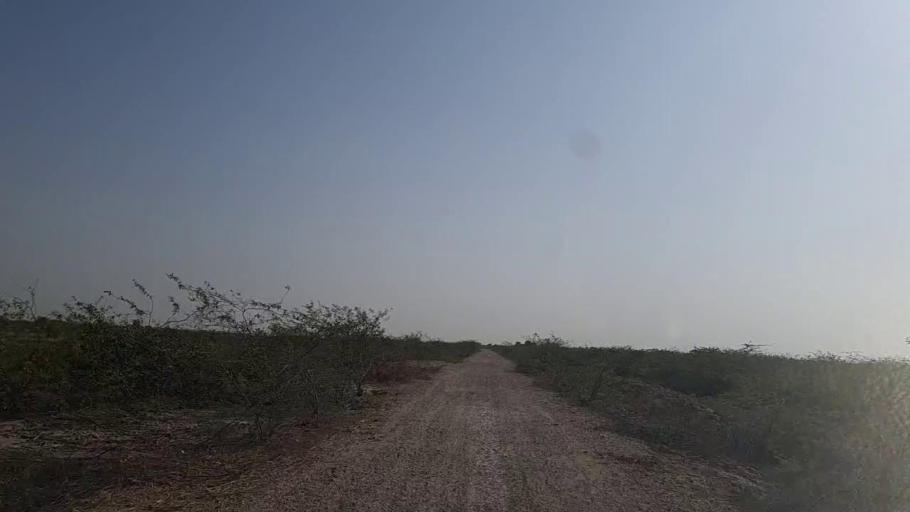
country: PK
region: Sindh
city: Naukot
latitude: 24.5963
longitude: 69.2635
